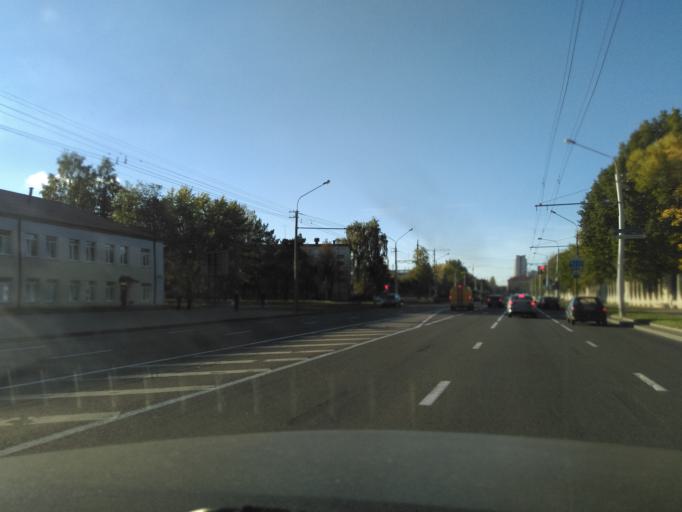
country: BY
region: Minsk
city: Minsk
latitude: 53.9098
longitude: 27.6103
